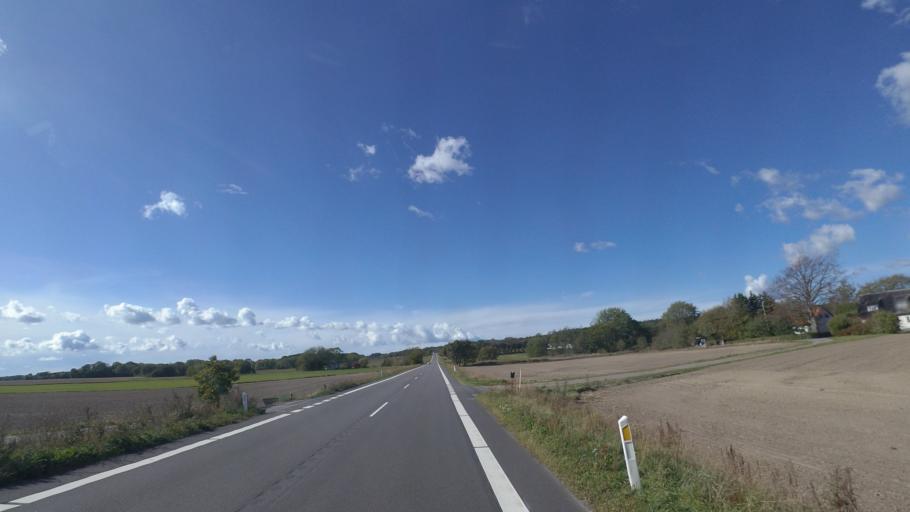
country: DK
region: Capital Region
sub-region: Bornholm Kommune
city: Nexo
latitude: 55.0608
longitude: 15.0472
